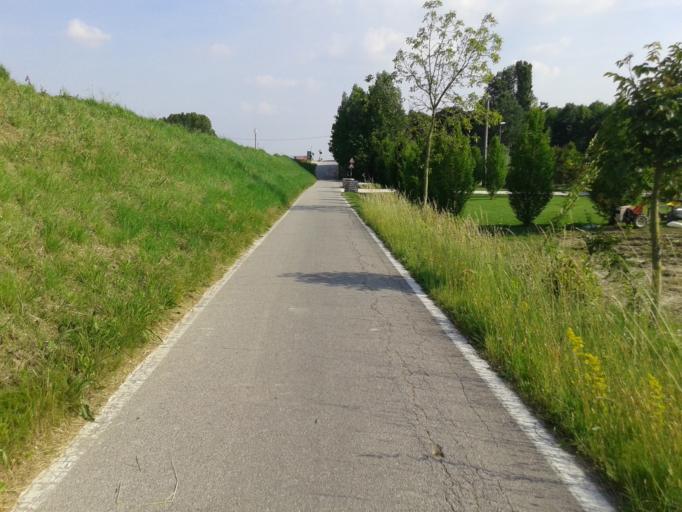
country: IT
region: Veneto
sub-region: Provincia di Padova
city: Loreggia
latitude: 45.5955
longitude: 11.9356
